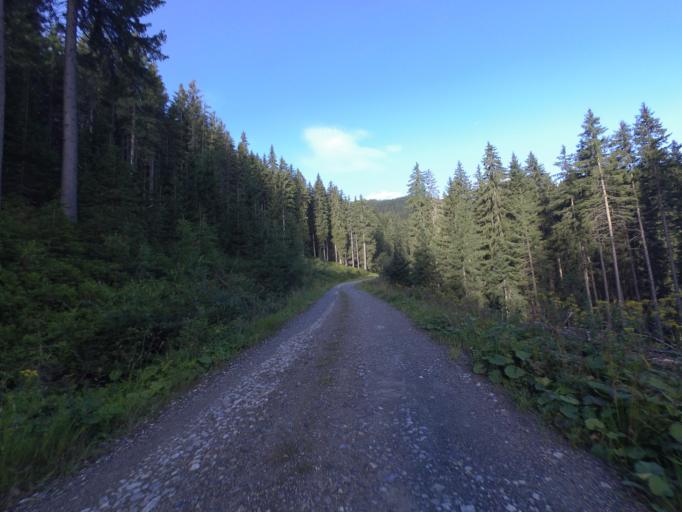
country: AT
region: Salzburg
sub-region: Politischer Bezirk Sankt Johann im Pongau
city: Goldegg
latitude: 47.3531
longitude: 13.1015
